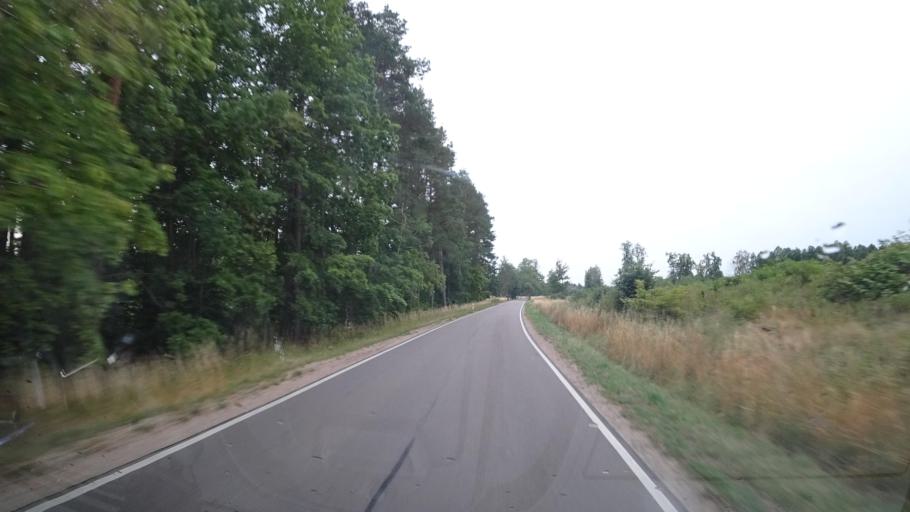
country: PL
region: Warmian-Masurian Voivodeship
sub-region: Powiat gizycki
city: Ryn
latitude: 53.8808
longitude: 21.5818
